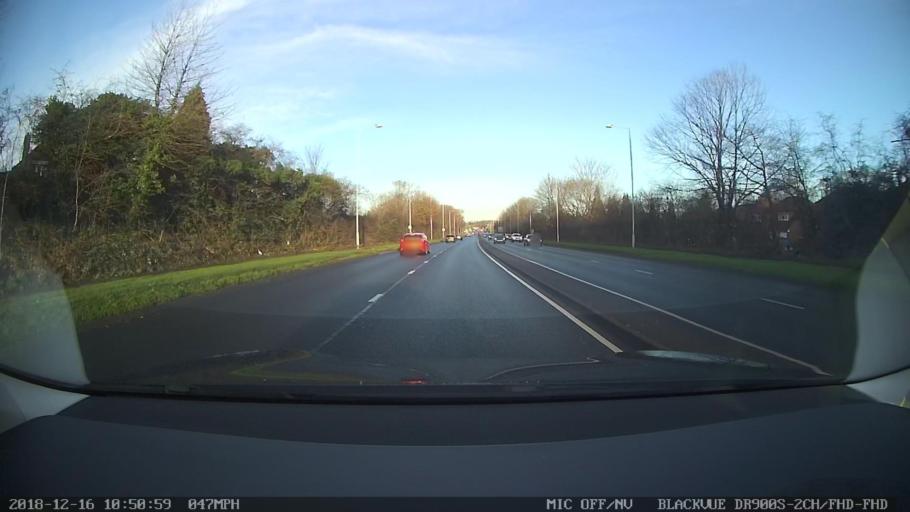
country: GB
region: England
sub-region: Manchester
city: Didsbury
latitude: 53.3841
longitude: -2.2228
